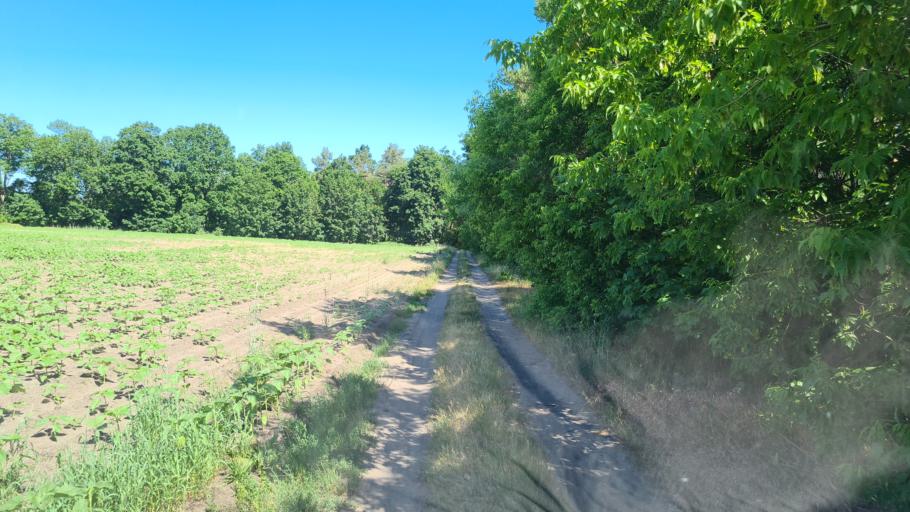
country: DE
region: Brandenburg
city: Plessa
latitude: 51.4706
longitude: 13.6417
